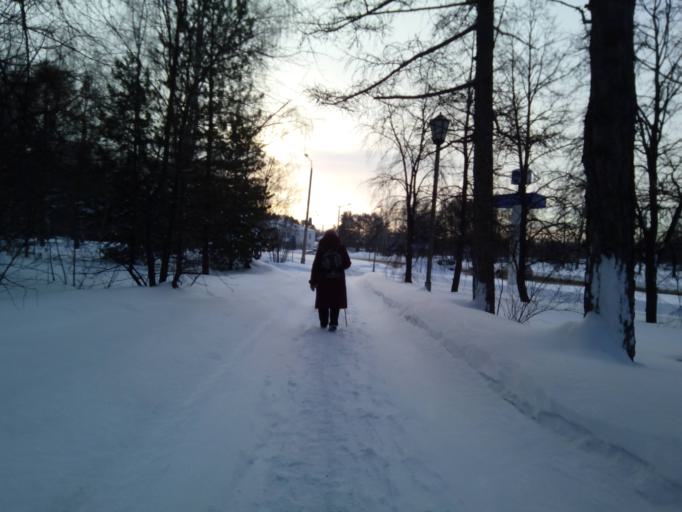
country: RU
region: Novosibirsk
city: Akademgorodok
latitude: 54.8460
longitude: 83.1120
